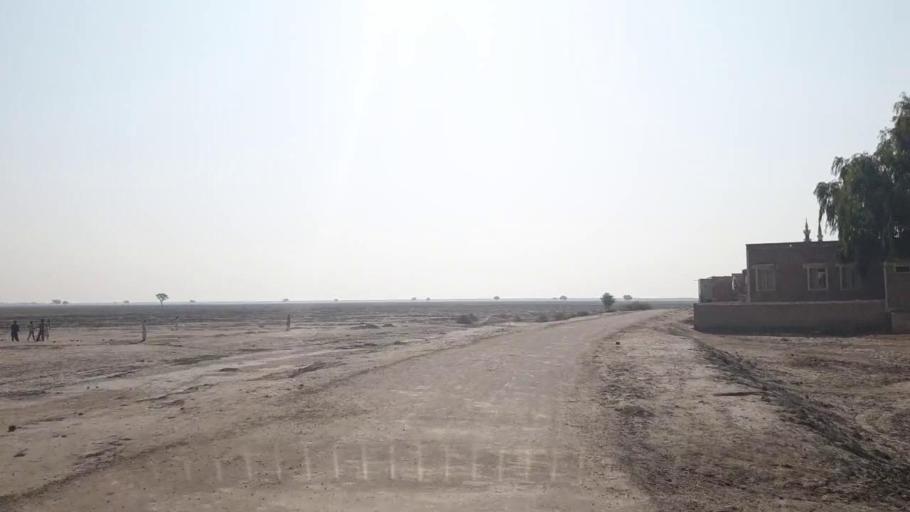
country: PK
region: Sindh
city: Bhan
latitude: 26.4360
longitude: 67.7354
